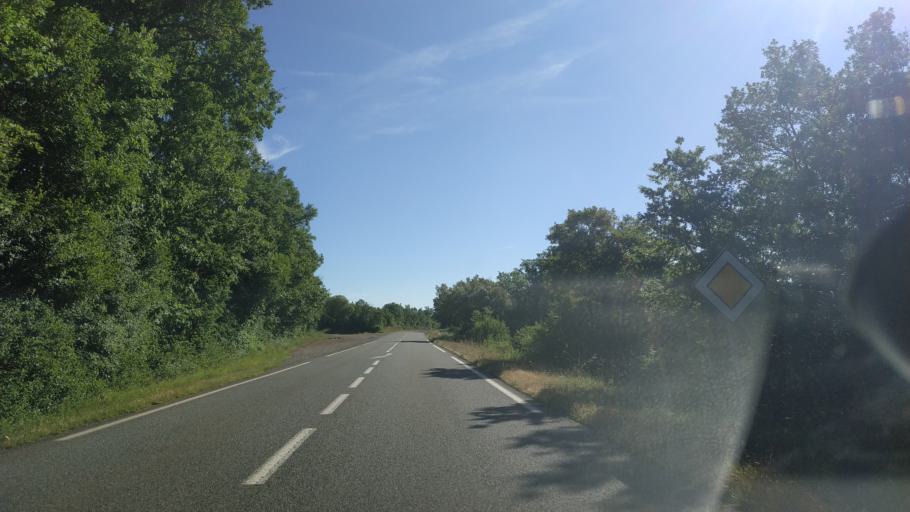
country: FR
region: Midi-Pyrenees
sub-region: Departement du Lot
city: Lacapelle-Marival
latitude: 44.6614
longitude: 1.8570
